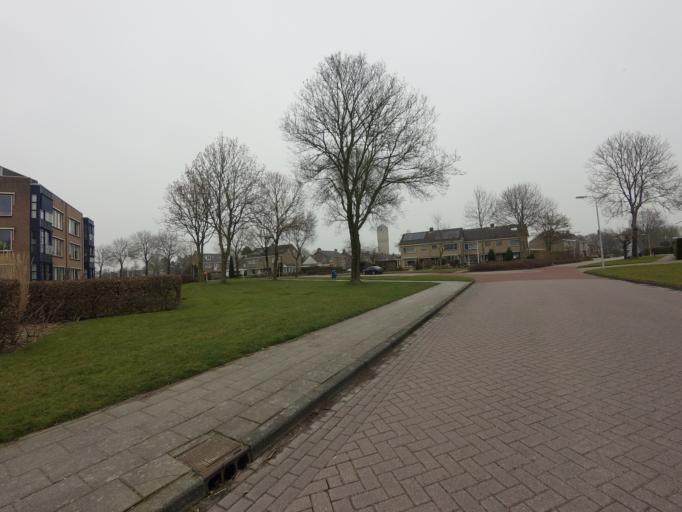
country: NL
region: Friesland
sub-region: Gemeente Franekeradeel
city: Franeker
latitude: 53.1863
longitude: 5.5546
